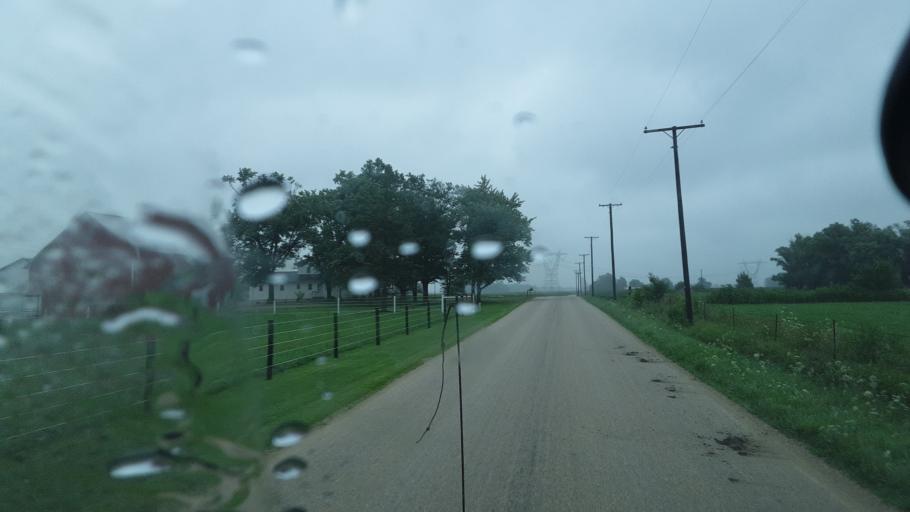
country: US
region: Indiana
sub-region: Adams County
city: Berne
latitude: 40.6874
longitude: -84.9399
